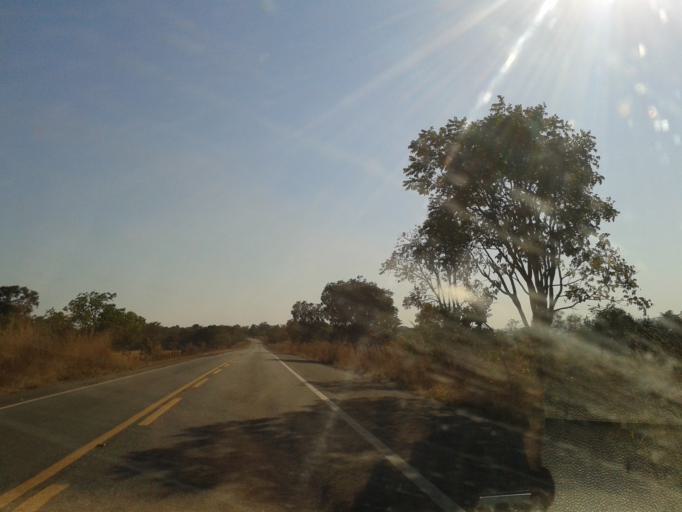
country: BR
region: Goias
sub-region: Mozarlandia
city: Mozarlandia
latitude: -14.9140
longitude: -50.5509
